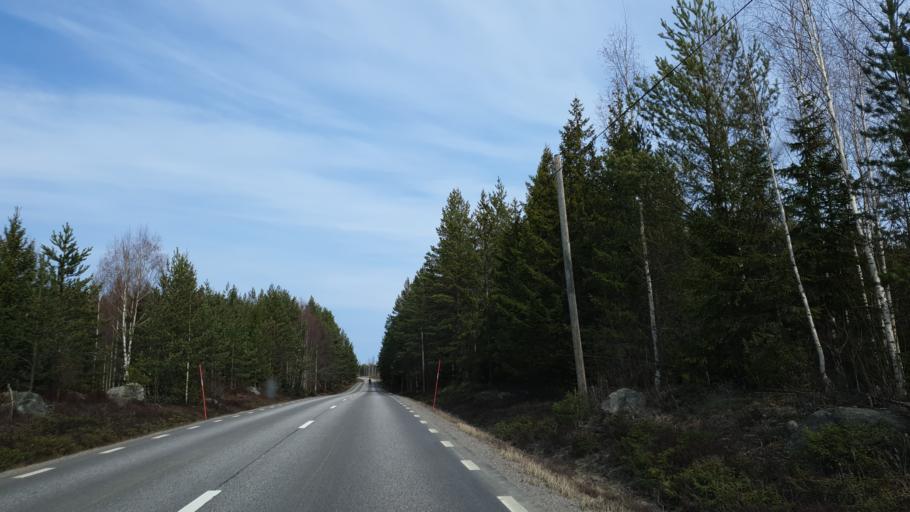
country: SE
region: Gaevleborg
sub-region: Gavle Kommun
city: Norrsundet
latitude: 61.0117
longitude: 17.1371
